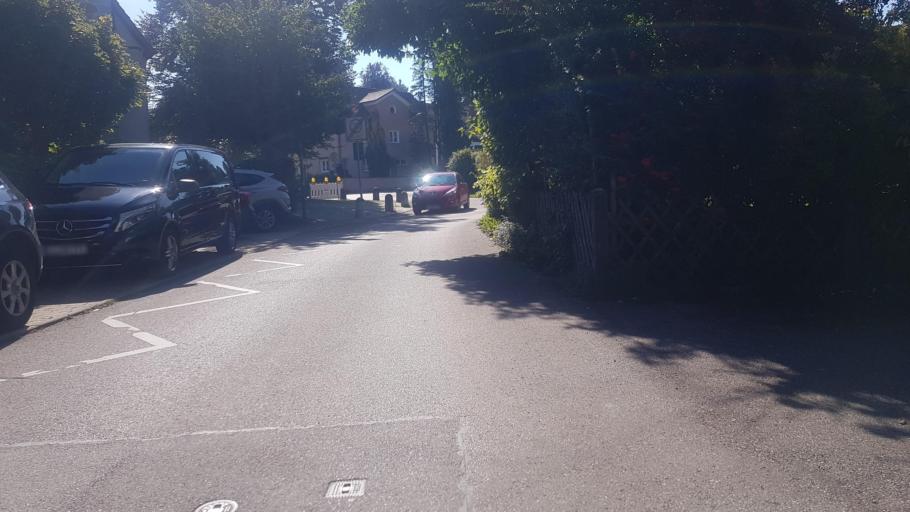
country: DE
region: Bavaria
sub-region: Swabia
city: Bodolz
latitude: 47.5607
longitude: 9.6684
